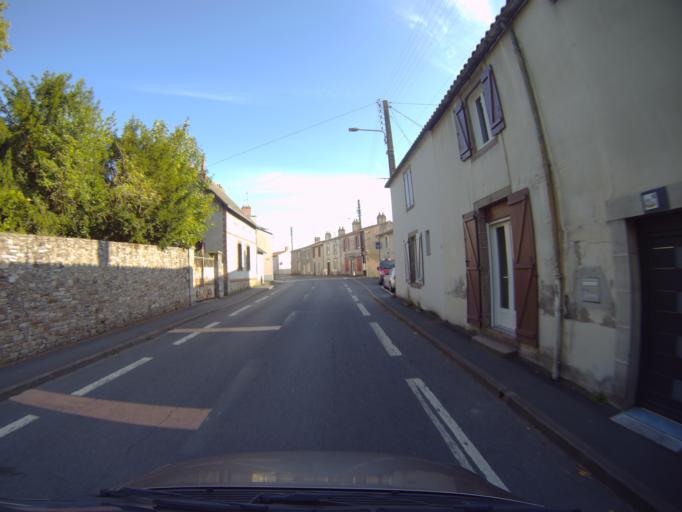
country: FR
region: Pays de la Loire
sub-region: Departement de la Vendee
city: Montaigu
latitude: 46.9728
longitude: -1.3121
